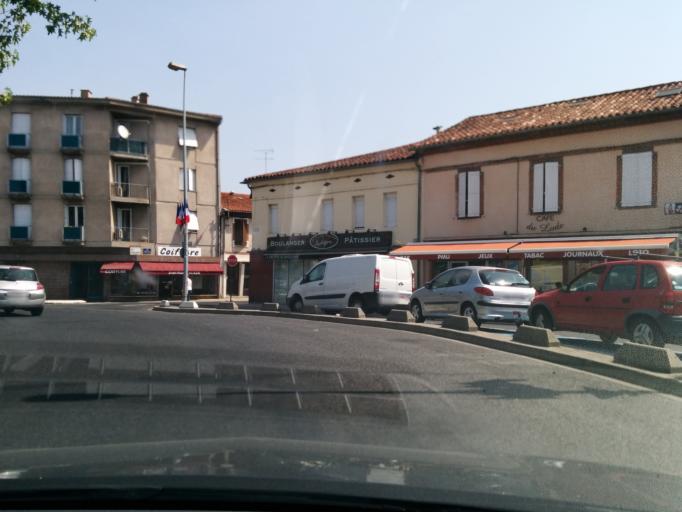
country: FR
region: Midi-Pyrenees
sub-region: Departement du Tarn
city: Albi
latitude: 43.9220
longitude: 2.1494
